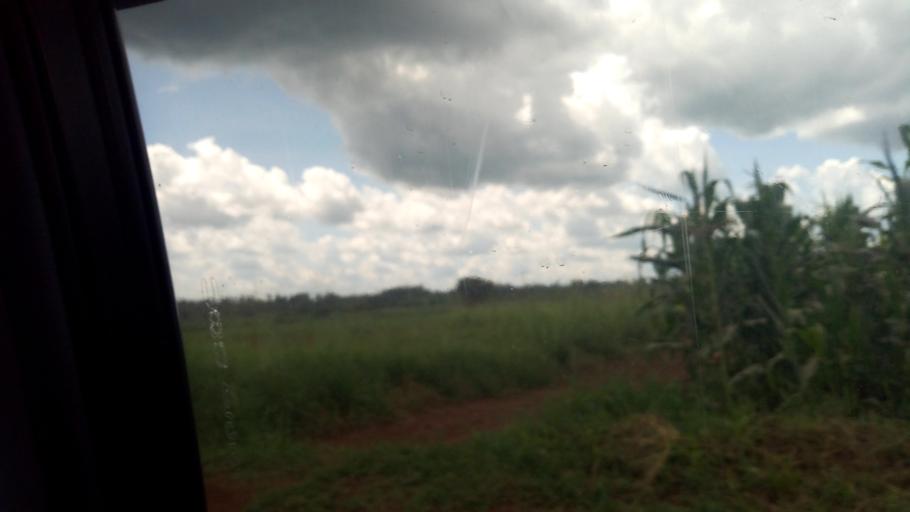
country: UG
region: Western Region
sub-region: Kiryandongo District
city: Kiryandongo
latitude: 1.9242
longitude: 32.1352
